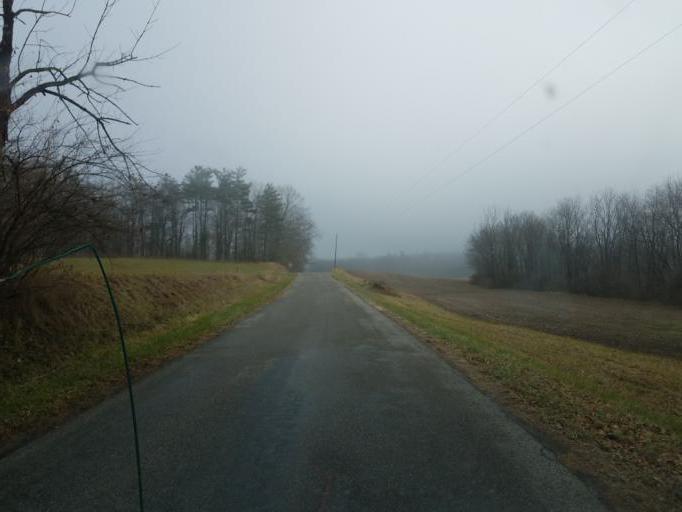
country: US
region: Ohio
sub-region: Champaign County
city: North Lewisburg
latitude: 40.2862
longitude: -83.6171
